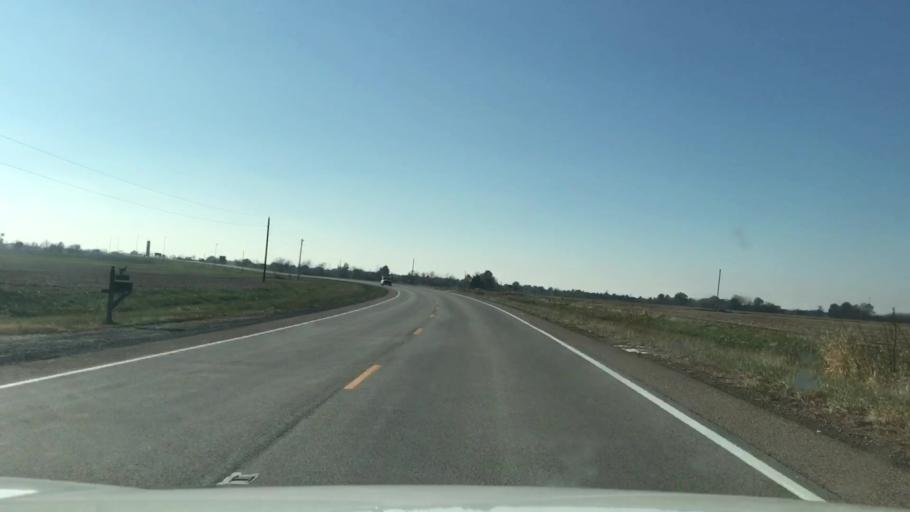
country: US
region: Illinois
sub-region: Washington County
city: Okawville
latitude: 38.4428
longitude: -89.5210
